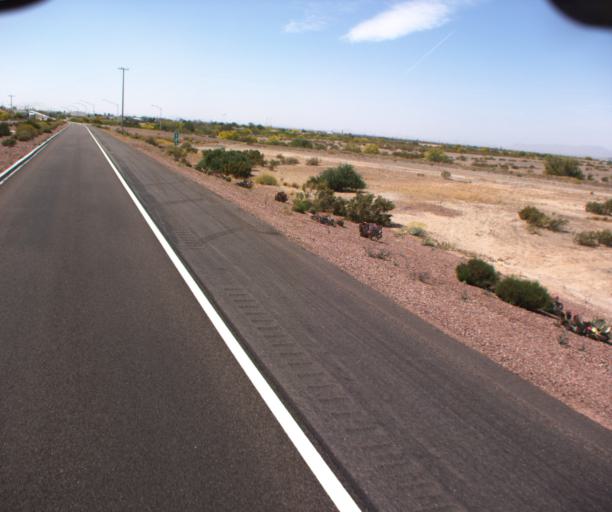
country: US
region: Arizona
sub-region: Maricopa County
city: Gila Bend
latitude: 32.9536
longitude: -112.6881
